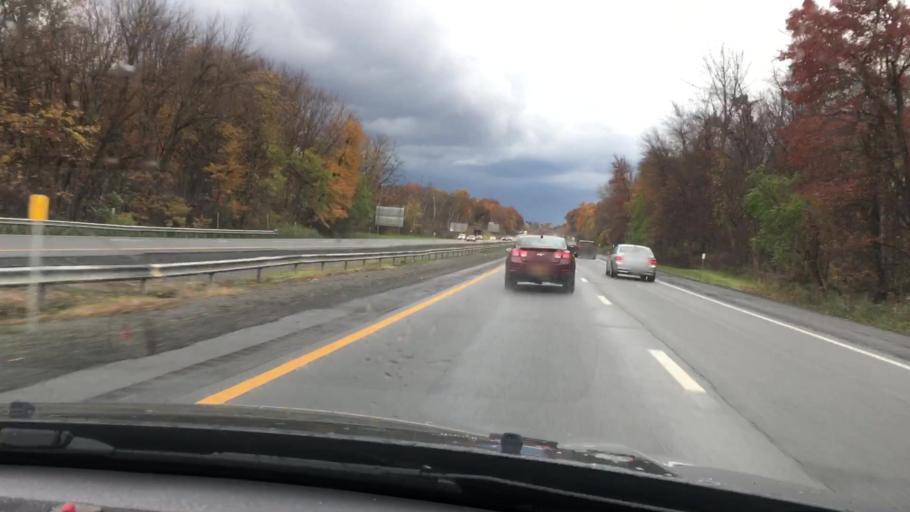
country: US
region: New York
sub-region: Orange County
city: Gardnertown
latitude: 41.4987
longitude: -74.0774
